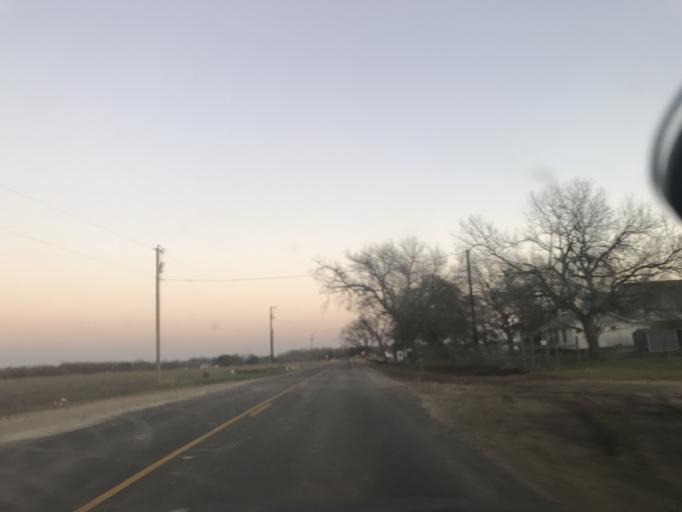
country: US
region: Texas
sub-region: Williamson County
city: Hutto
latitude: 30.4993
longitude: -97.5063
